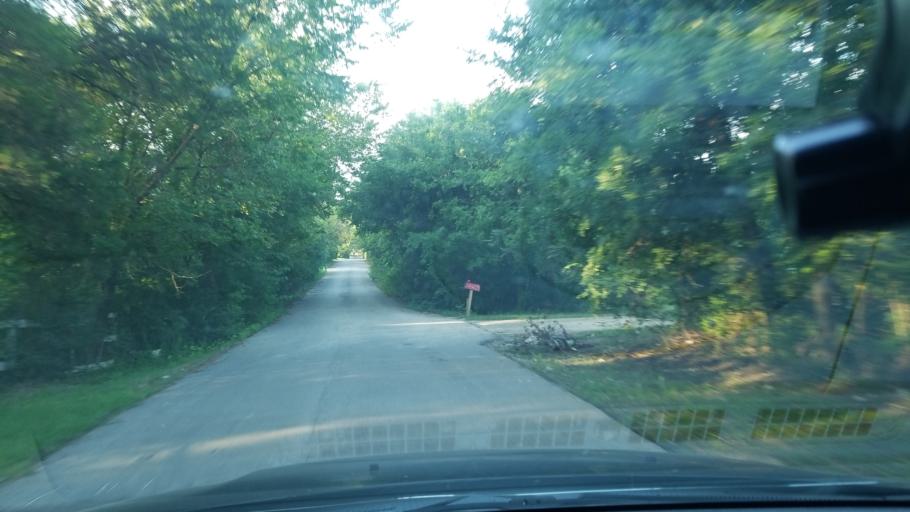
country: US
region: Texas
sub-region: Dallas County
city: Balch Springs
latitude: 32.7217
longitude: -96.6649
